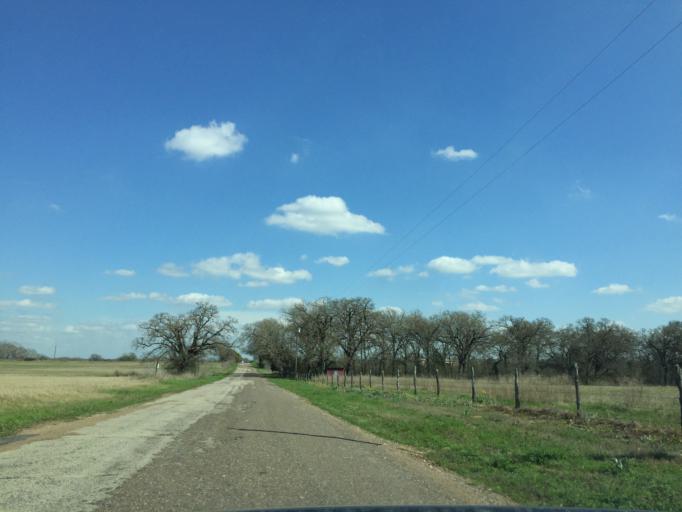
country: US
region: Texas
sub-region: Milam County
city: Thorndale
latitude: 30.5560
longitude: -97.1633
